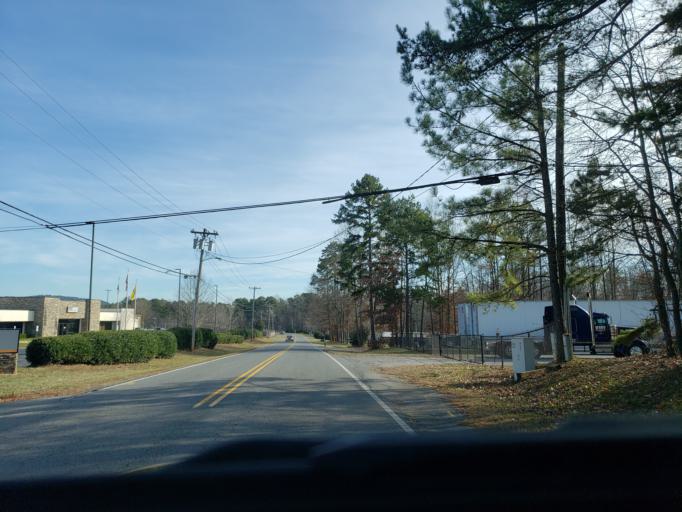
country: US
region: North Carolina
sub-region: Cleveland County
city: Kings Mountain
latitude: 35.2398
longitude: -81.3237
